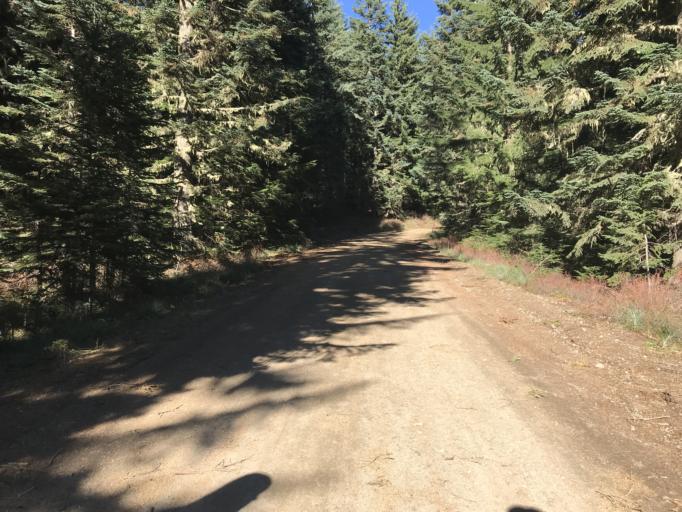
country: US
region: Washington
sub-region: King County
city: Enumclaw
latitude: 47.0365
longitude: -121.5971
